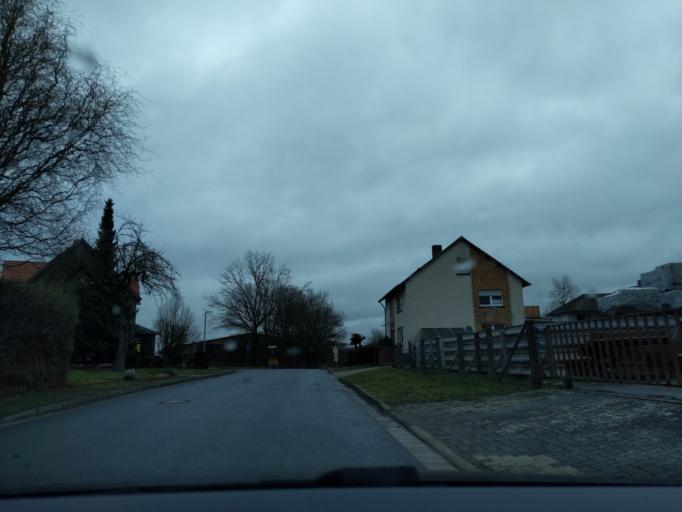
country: DE
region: Hesse
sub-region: Regierungsbezirk Kassel
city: Volkmarsen
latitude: 51.3485
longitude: 9.0869
